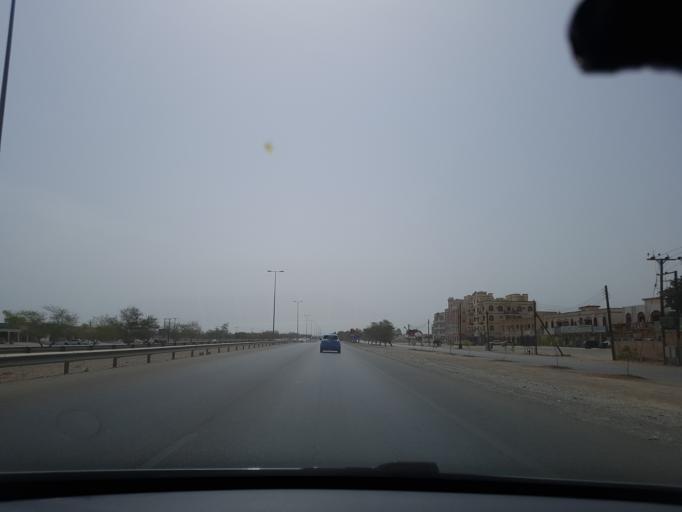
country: OM
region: Al Batinah
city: As Suwayq
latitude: 23.8327
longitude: 57.3965
